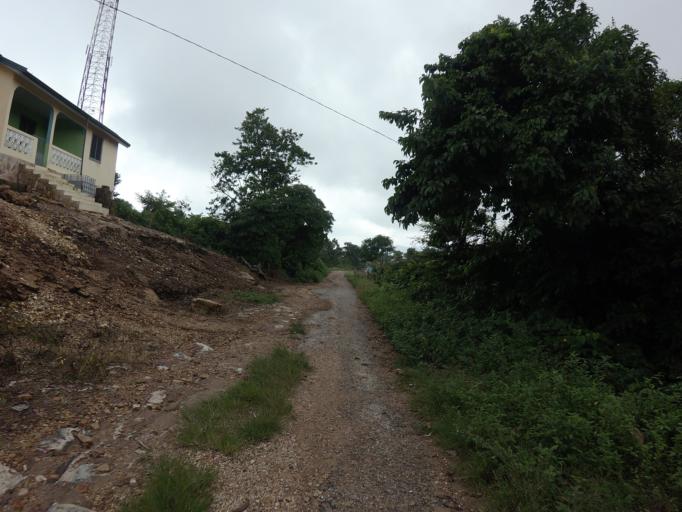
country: GH
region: Volta
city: Kpandu
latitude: 6.8422
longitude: 0.4336
